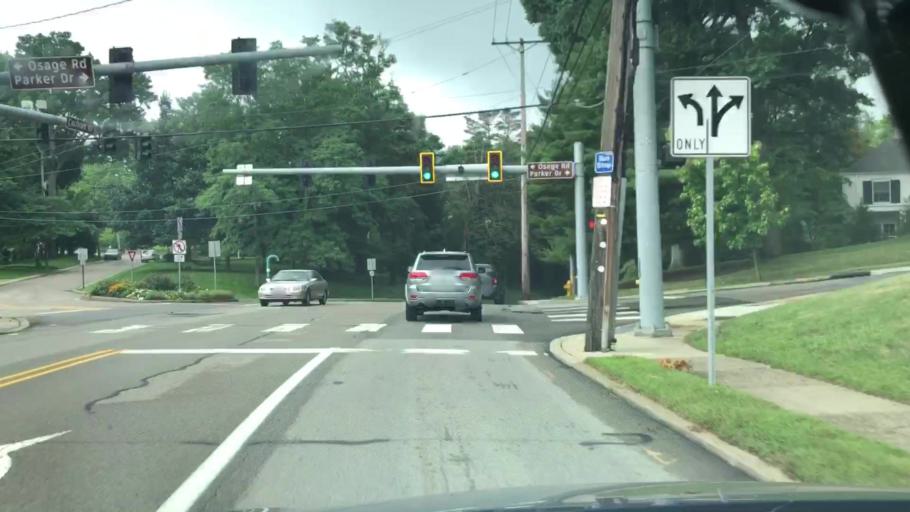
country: US
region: Pennsylvania
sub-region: Allegheny County
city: Dormont
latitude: 40.3884
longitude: -80.0568
